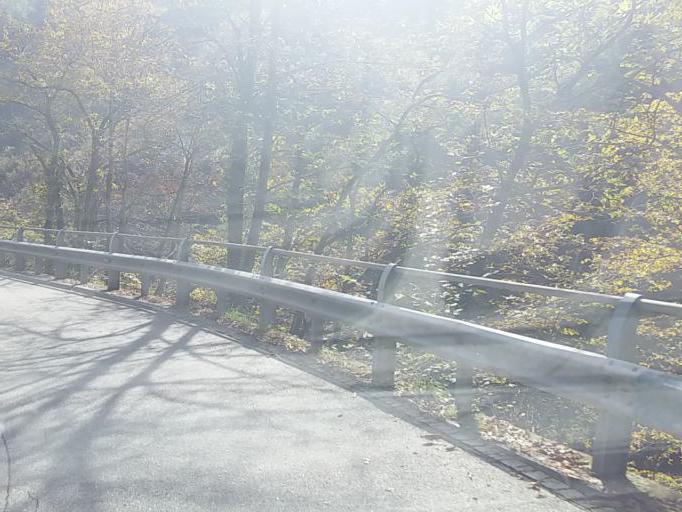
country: IT
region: Piedmont
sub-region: Provincia Verbano-Cusio-Ossola
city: Cavaglio-Spoccia
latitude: 46.0690
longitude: 8.6152
